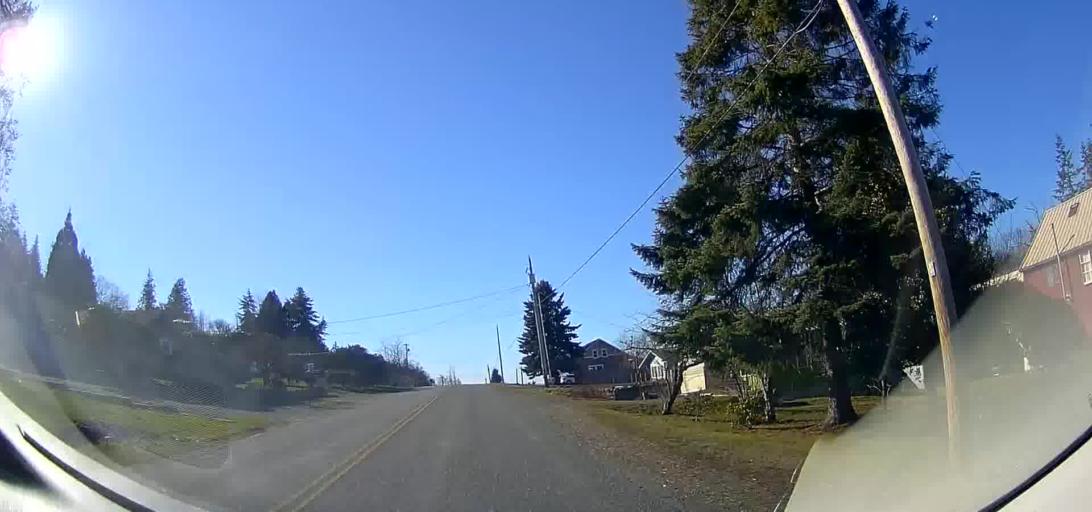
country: US
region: Washington
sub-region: Skagit County
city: Clear Lake
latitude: 48.4570
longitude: -122.2461
